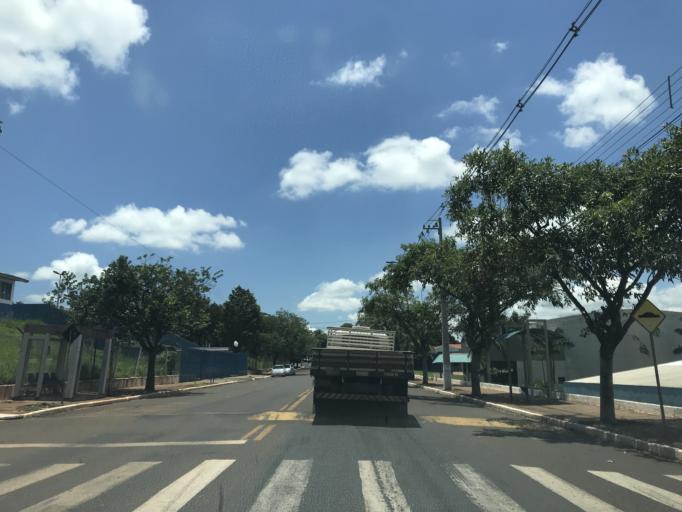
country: BR
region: Parana
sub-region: Marialva
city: Marialva
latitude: -23.4902
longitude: -51.7890
